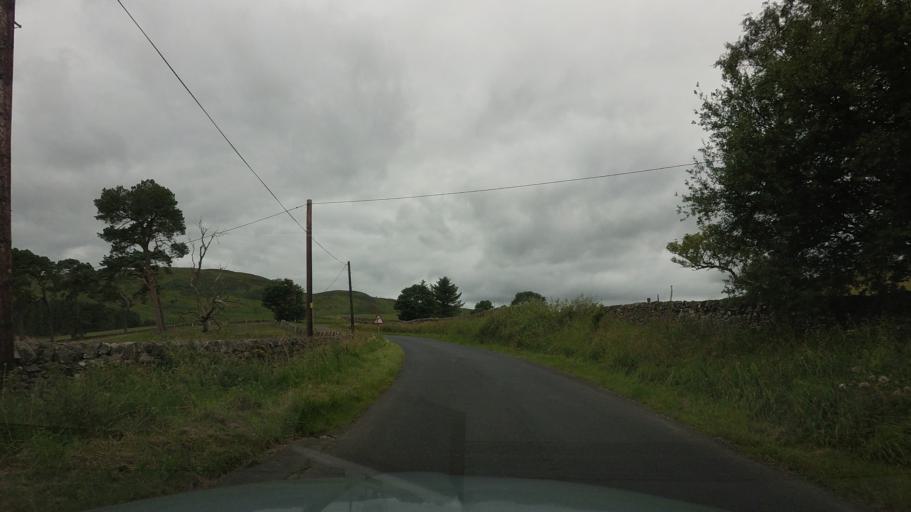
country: GB
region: Scotland
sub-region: The Scottish Borders
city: Innerleithen
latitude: 55.4814
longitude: -3.0121
